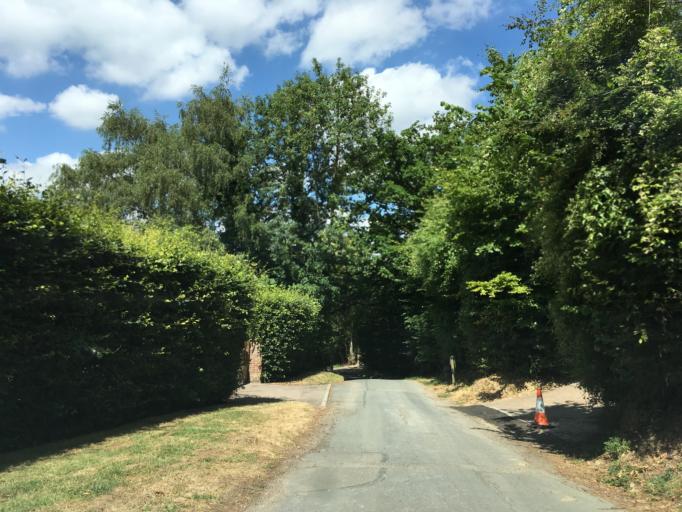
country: GB
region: England
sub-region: Gloucestershire
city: Shurdington
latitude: 51.8445
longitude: -2.1177
